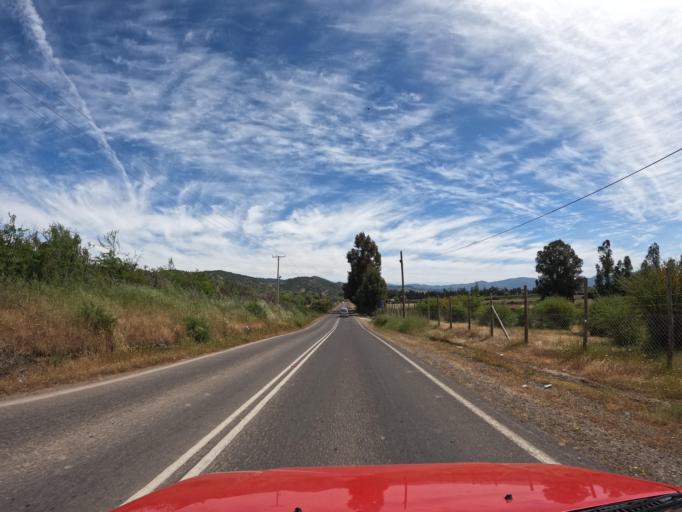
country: CL
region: Maule
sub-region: Provincia de Talca
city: Talca
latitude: -35.1129
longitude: -71.6343
